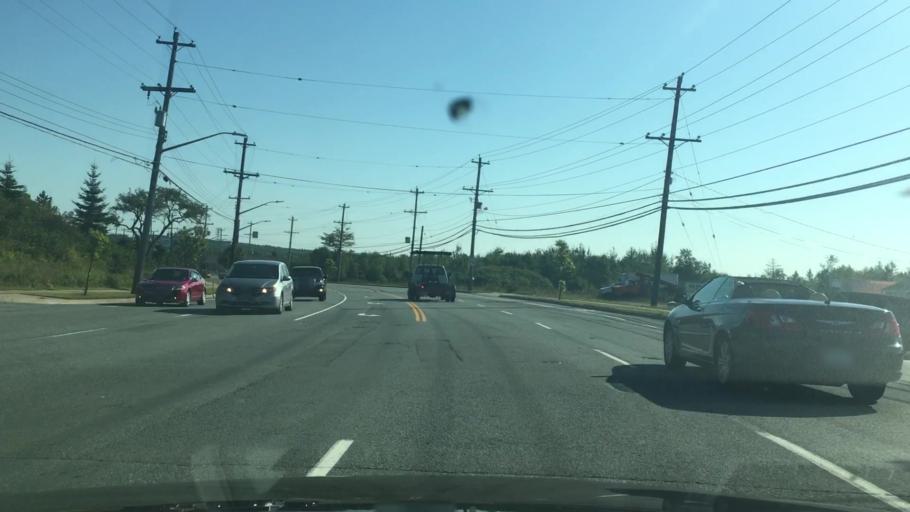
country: CA
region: Nova Scotia
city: Cole Harbour
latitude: 44.6984
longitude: -63.4868
